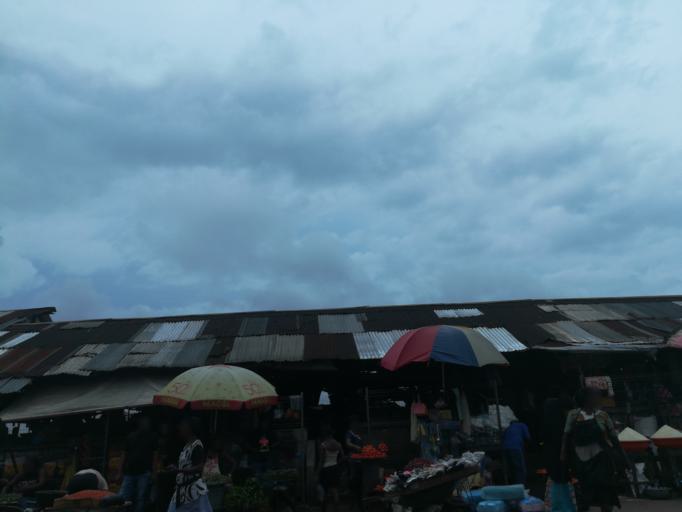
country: NG
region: Rivers
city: Port Harcourt
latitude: 4.7587
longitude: 7.0237
